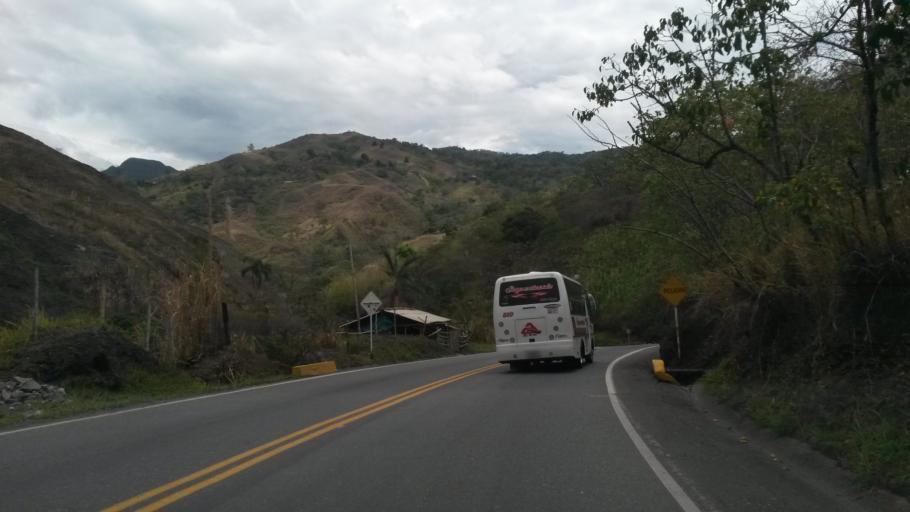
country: CO
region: Cauca
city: Rosas
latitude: 2.2771
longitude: -76.7093
